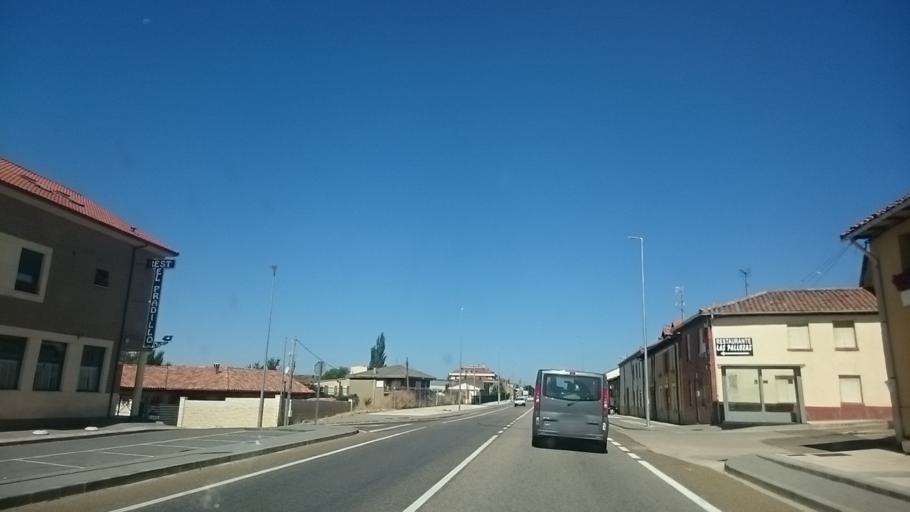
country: ES
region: Castille and Leon
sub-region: Provincia de Leon
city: Valdefresno
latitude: 42.5656
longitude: -5.4977
